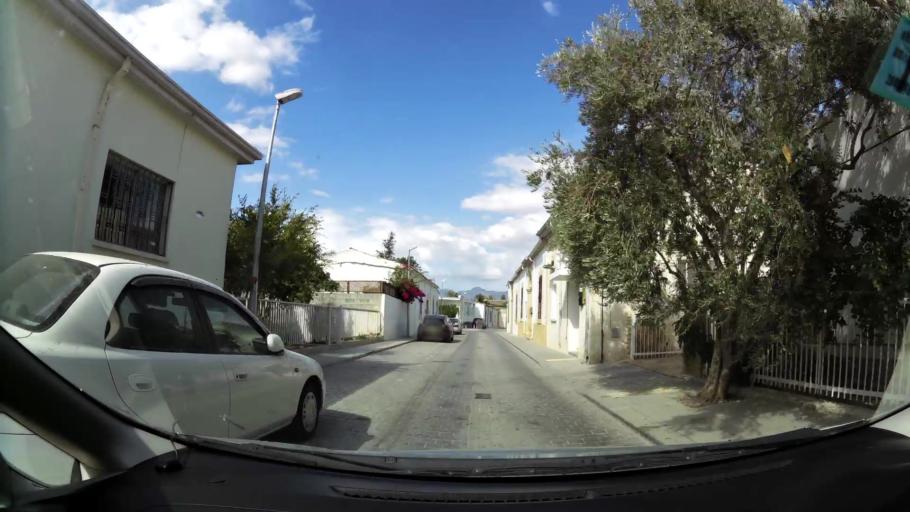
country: CY
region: Lefkosia
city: Nicosia
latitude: 35.1855
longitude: 33.3779
